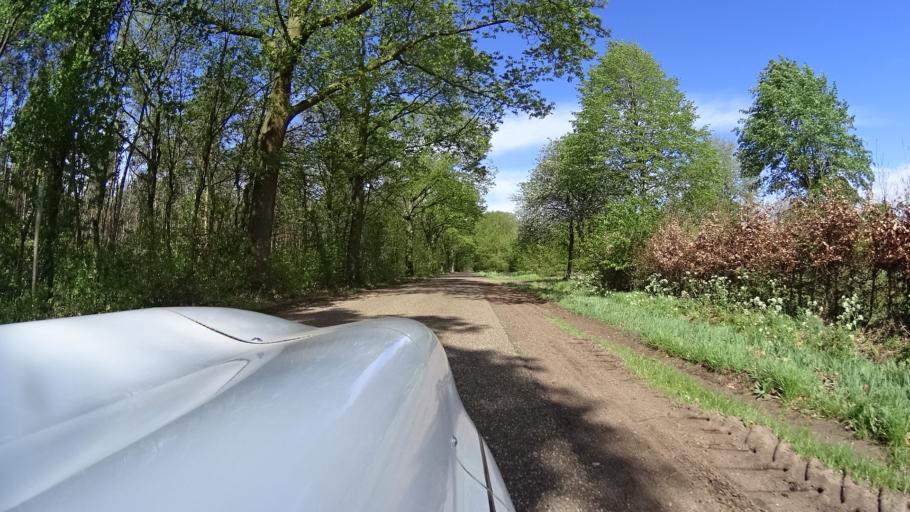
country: NL
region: North Brabant
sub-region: Gemeente Mill en Sint Hubert
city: Wilbertoord
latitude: 51.5960
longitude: 5.8109
